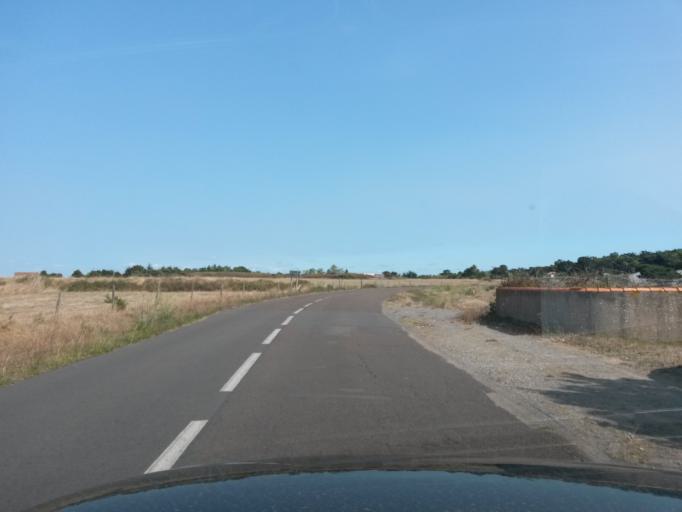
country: FR
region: Pays de la Loire
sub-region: Departement de la Vendee
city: Bretignolles-sur-Mer
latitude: 46.6137
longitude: -1.8530
